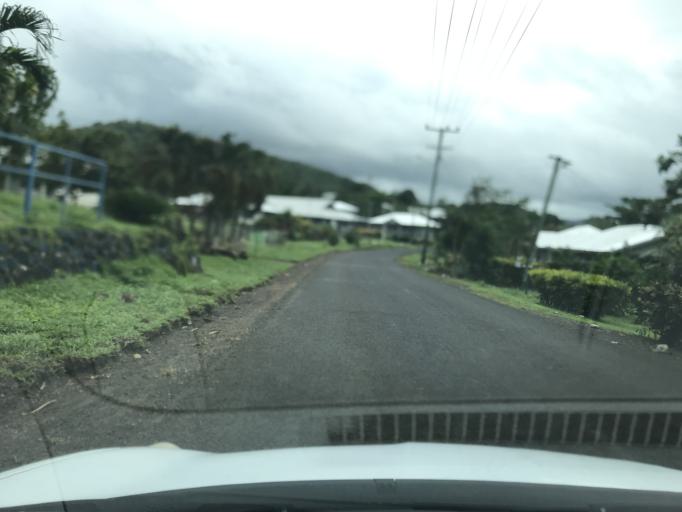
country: WS
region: Atua
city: Lufilufi
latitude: -13.8762
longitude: -171.6031
